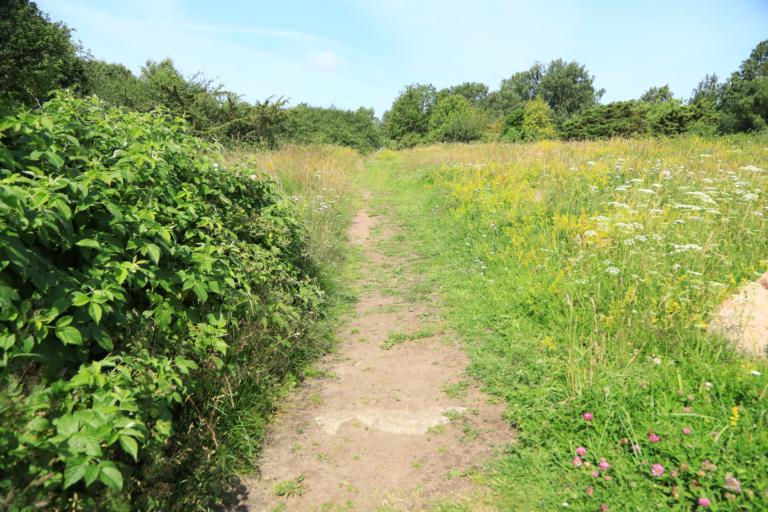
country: SE
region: Halland
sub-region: Varbergs Kommun
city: Varberg
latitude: 57.1282
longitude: 12.2759
